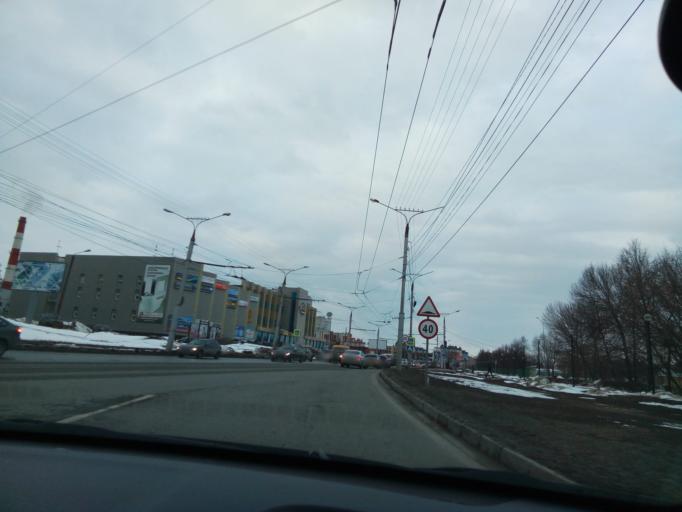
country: RU
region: Chuvashia
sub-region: Cheboksarskiy Rayon
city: Cheboksary
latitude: 56.1443
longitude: 47.2055
